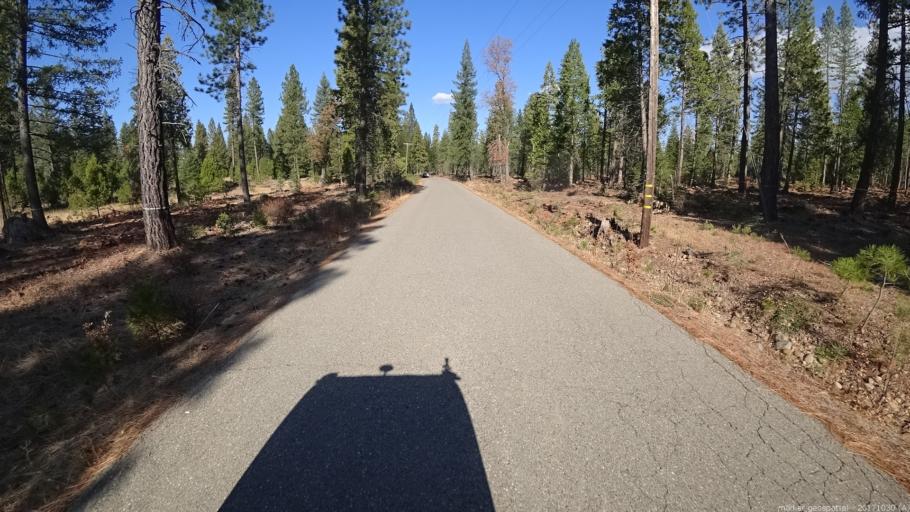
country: US
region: California
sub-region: Shasta County
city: Shingletown
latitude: 40.5131
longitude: -121.7262
